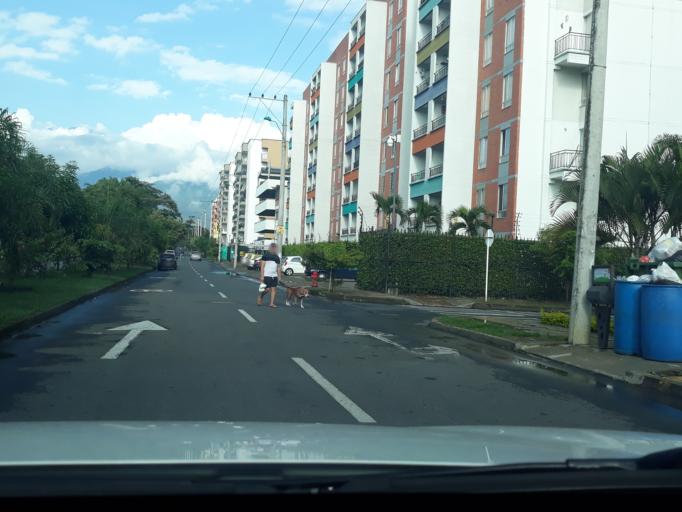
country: CO
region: Valle del Cauca
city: Cali
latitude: 3.3561
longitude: -76.5172
